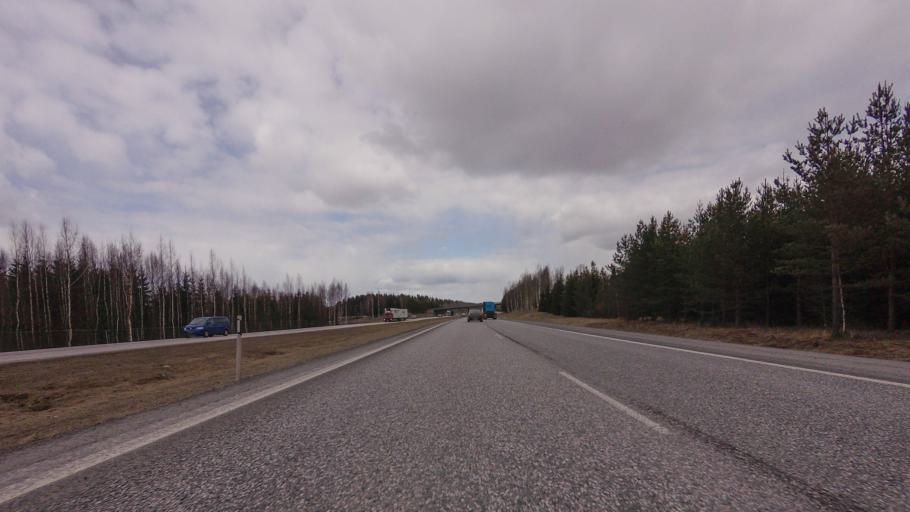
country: FI
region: Uusimaa
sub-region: Helsinki
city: Nurmijaervi
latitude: 60.3928
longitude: 24.8146
